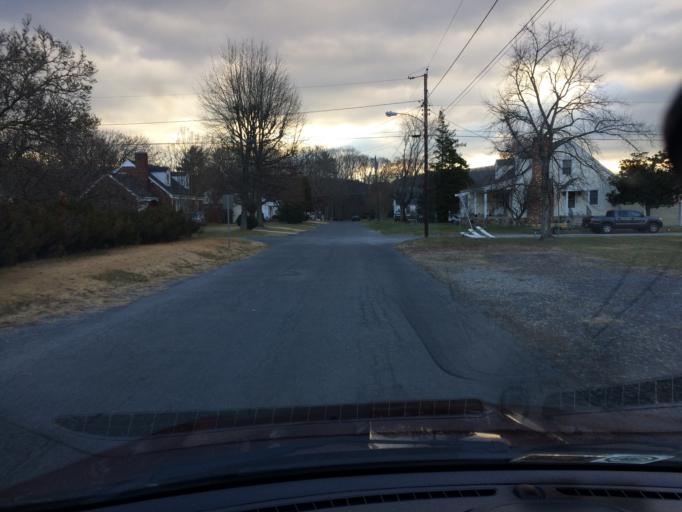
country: US
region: Virginia
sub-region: Alleghany County
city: Clifton Forge
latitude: 37.8247
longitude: -79.8197
